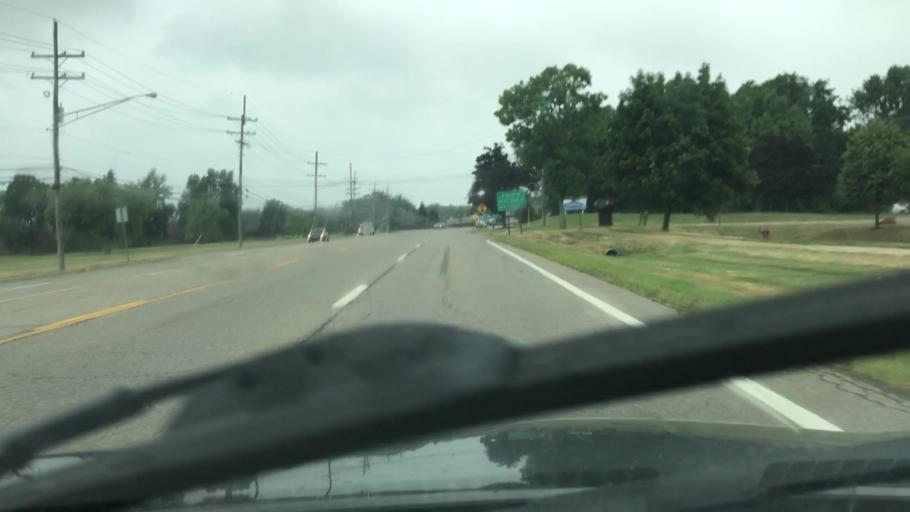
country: US
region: Michigan
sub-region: Oakland County
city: Wixom
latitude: 42.5192
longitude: -83.5374
